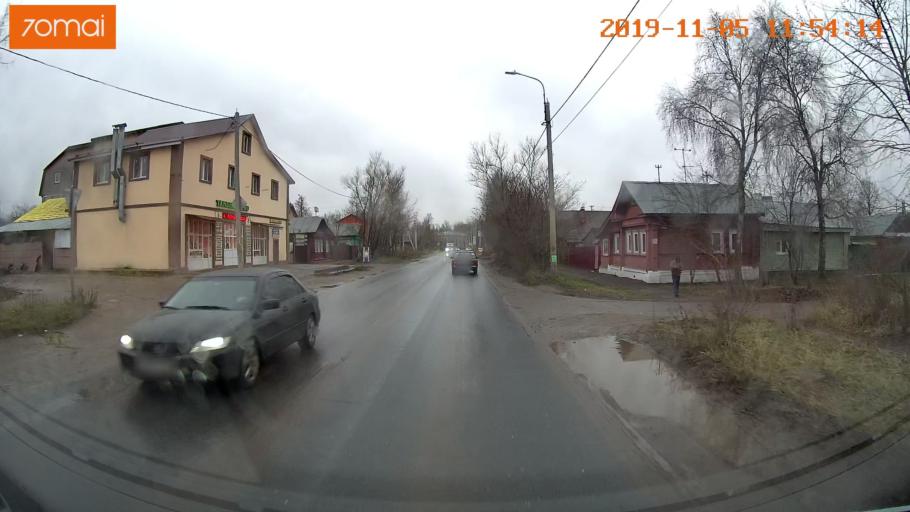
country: RU
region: Ivanovo
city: Bogorodskoye
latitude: 56.9919
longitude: 41.0311
